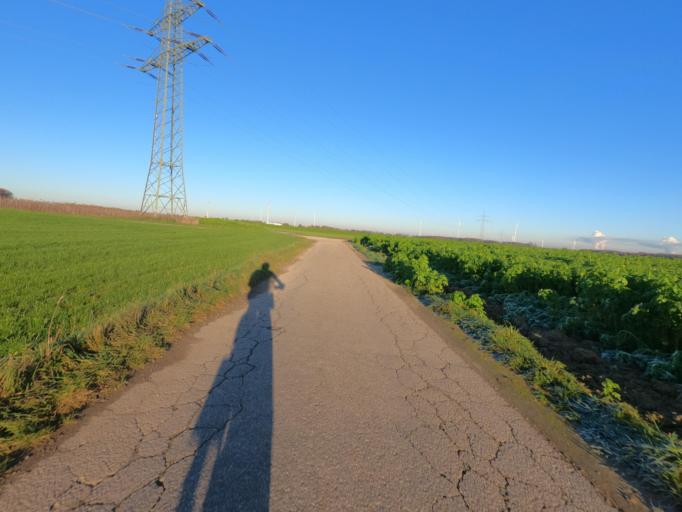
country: DE
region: North Rhine-Westphalia
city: Geilenkirchen
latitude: 51.0001
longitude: 6.0887
